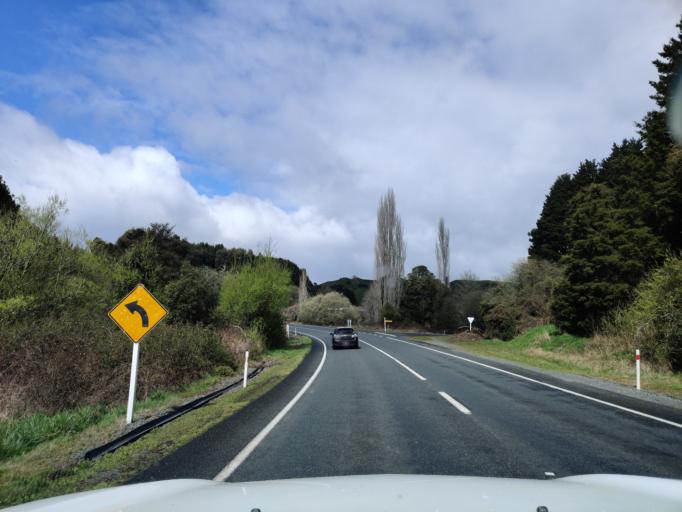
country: NZ
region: Waikato
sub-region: Otorohanga District
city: Otorohanga
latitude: -38.5843
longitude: 175.2155
